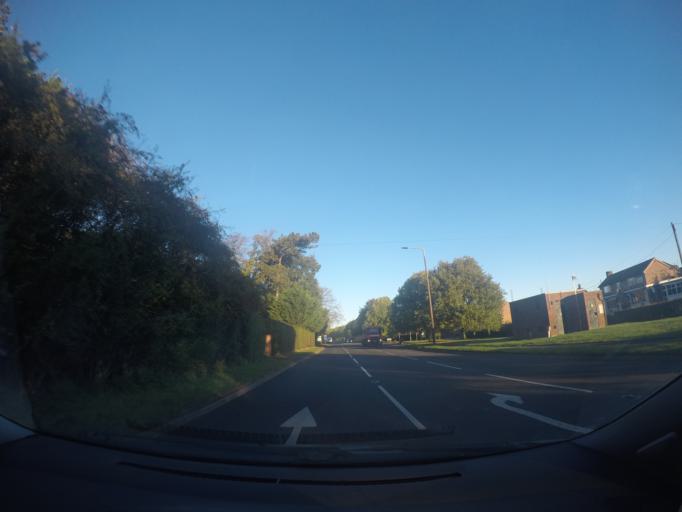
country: GB
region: England
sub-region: City of York
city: Skelton
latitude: 53.9827
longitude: -1.1179
